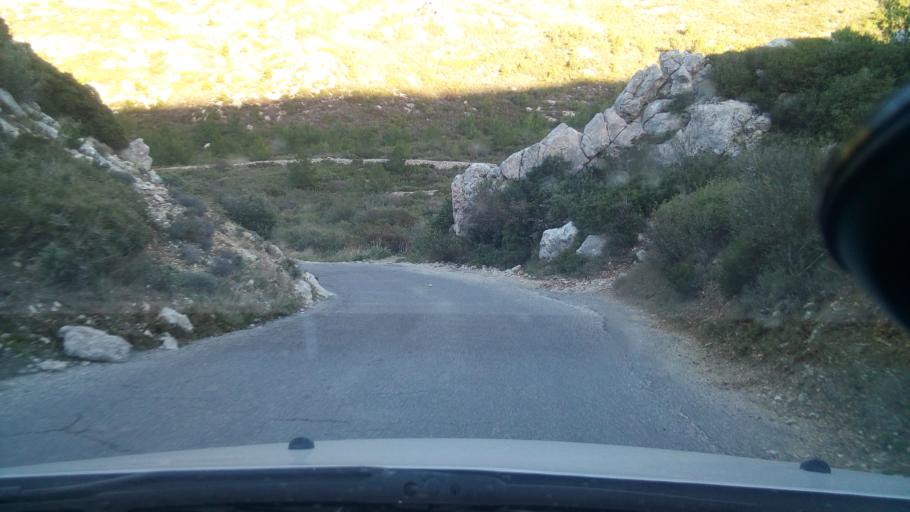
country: FR
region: Provence-Alpes-Cote d'Azur
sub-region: Departement des Bouches-du-Rhone
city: Marseille 09
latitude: 43.2180
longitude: 5.4071
